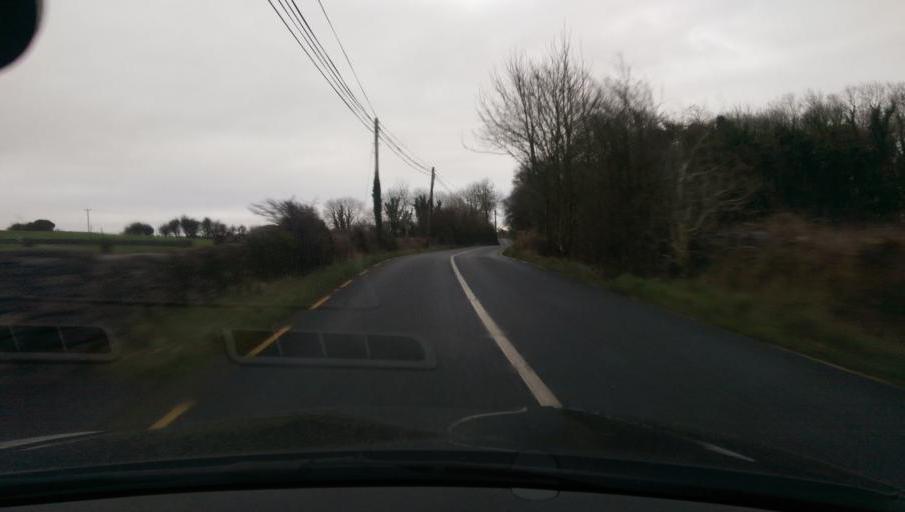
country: IE
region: Connaught
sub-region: County Galway
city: Athenry
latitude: 53.3071
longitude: -8.7833
